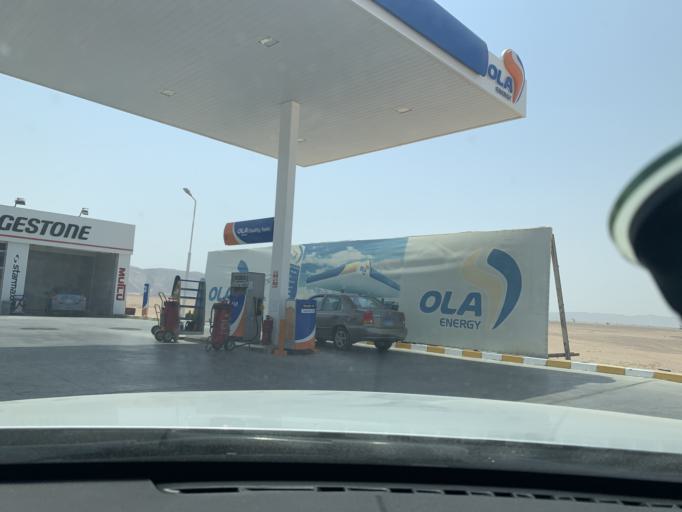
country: EG
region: Red Sea
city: El Gouna
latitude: 27.3676
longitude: 33.6626
